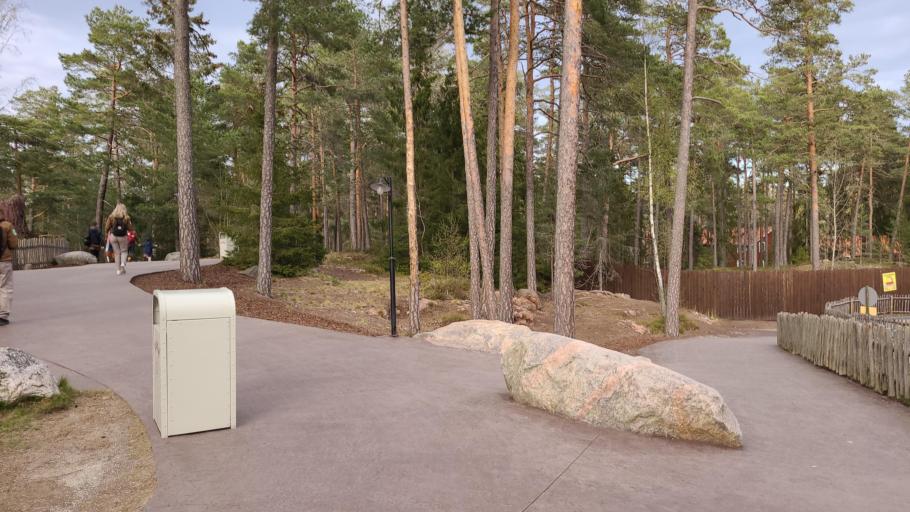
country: SE
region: OEstergoetland
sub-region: Norrkopings Kommun
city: Krokek
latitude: 58.6632
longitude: 16.4613
